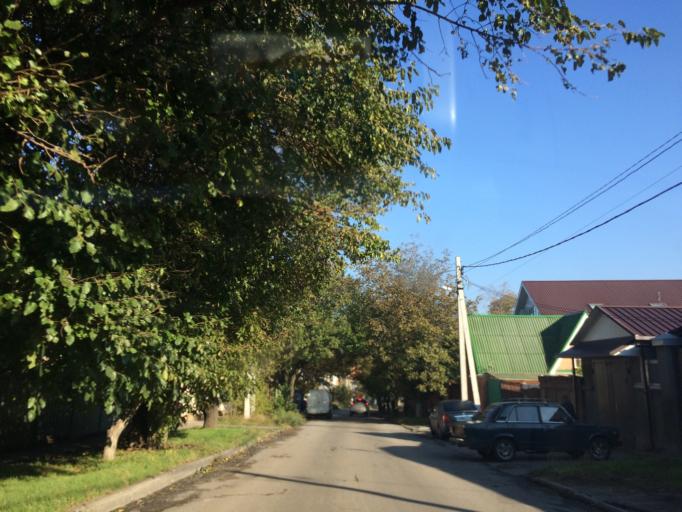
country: RU
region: Rostov
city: Rostov-na-Donu
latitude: 47.2176
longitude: 39.6633
